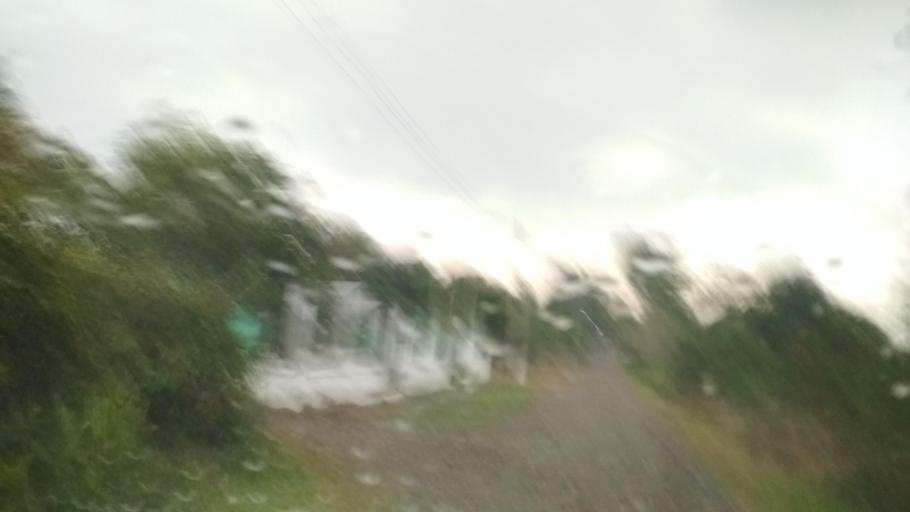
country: MM
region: Shan
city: Taunggyi
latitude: 20.3036
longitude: 97.3050
